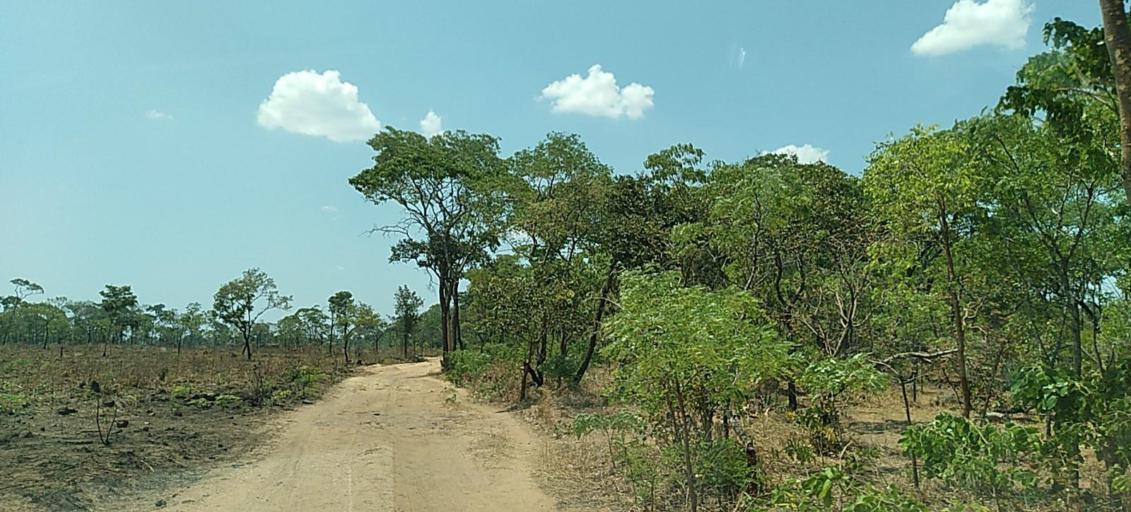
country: ZM
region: Copperbelt
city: Mpongwe
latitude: -13.6541
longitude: 28.4882
